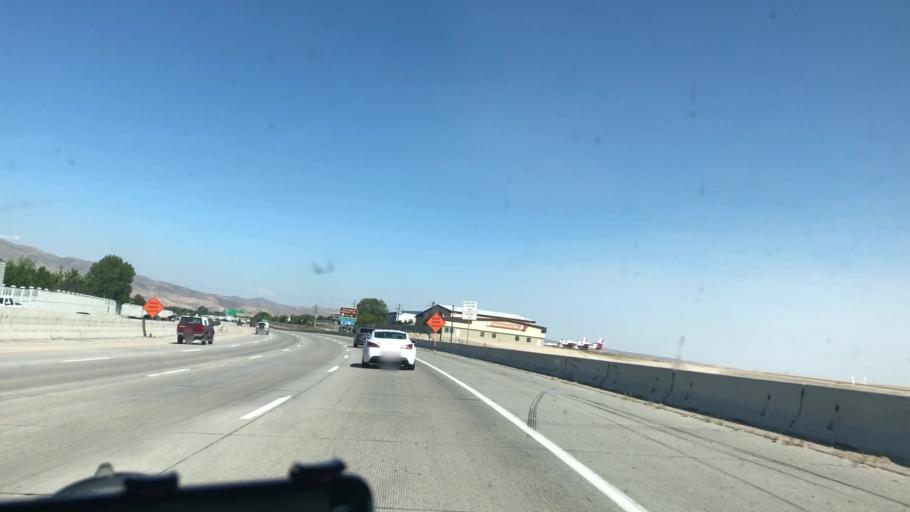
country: US
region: Idaho
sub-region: Ada County
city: Garden City
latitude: 43.5721
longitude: -116.2362
